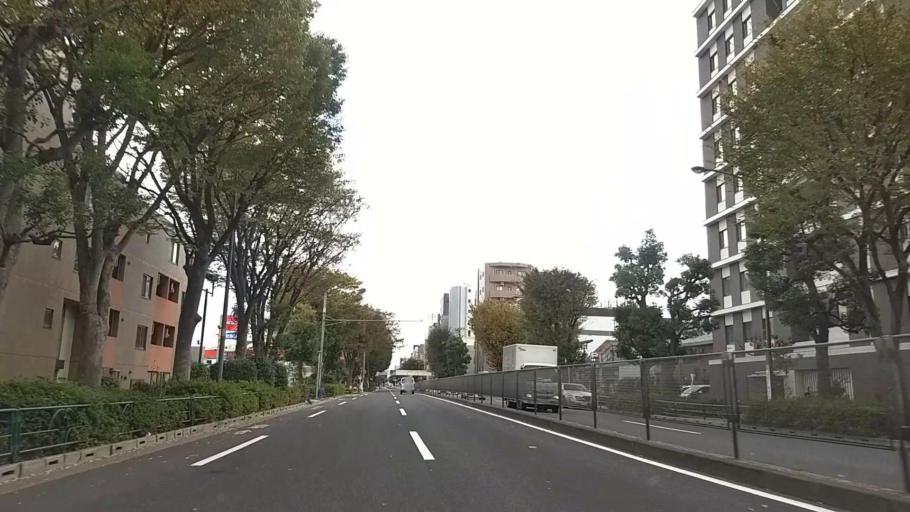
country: JP
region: Tokyo
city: Tokyo
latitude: 35.6123
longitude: 139.6885
